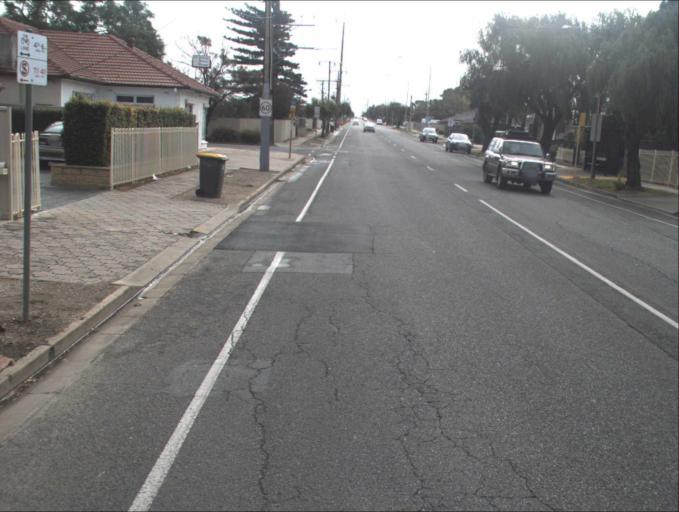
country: AU
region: South Australia
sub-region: Port Adelaide Enfield
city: Klemzig
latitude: -34.8666
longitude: 138.6368
